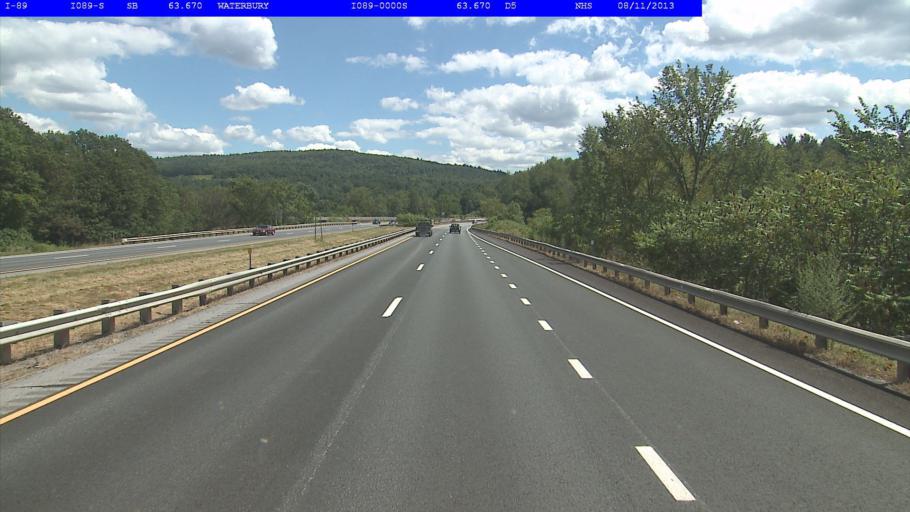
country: US
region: Vermont
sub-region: Washington County
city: Waterbury
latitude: 44.3424
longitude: -72.7511
